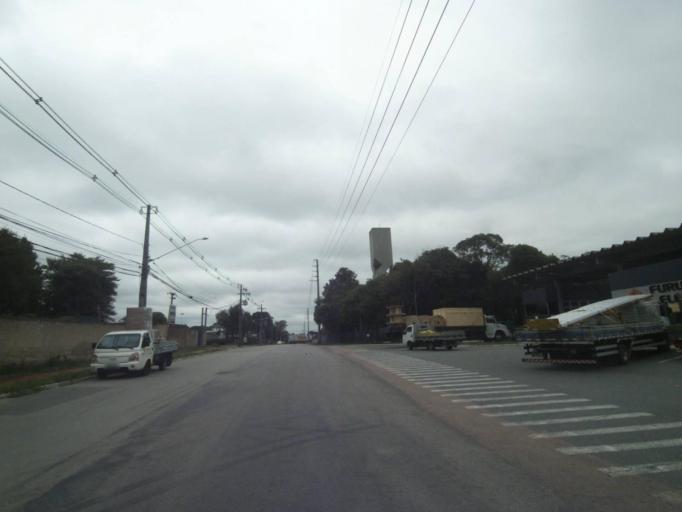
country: BR
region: Parana
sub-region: Sao Jose Dos Pinhais
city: Sao Jose dos Pinhais
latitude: -25.5552
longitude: -49.3084
